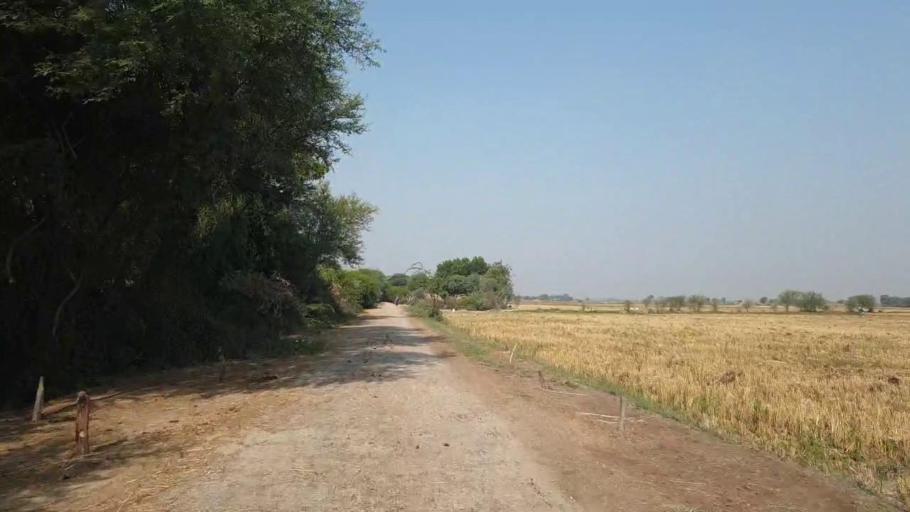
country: PK
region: Sindh
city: Matli
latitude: 24.9798
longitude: 68.6177
